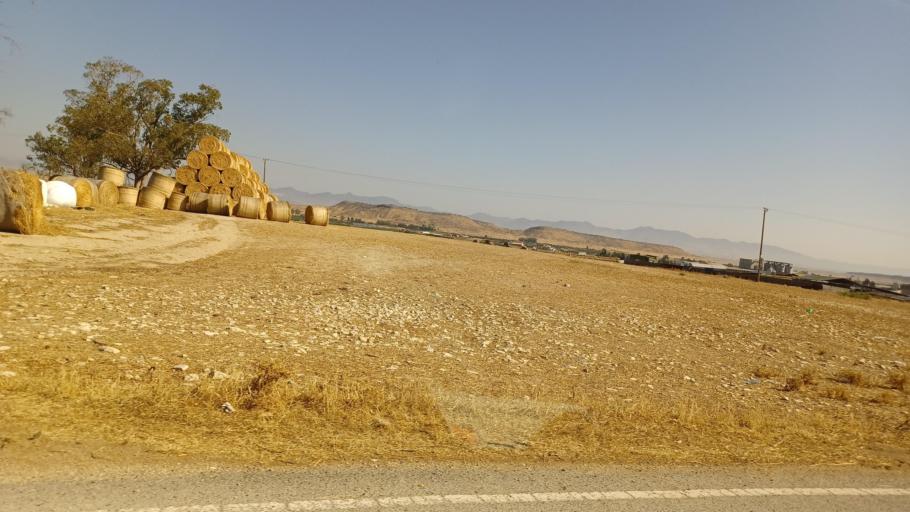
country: CY
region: Larnaka
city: Athienou
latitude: 35.0475
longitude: 33.5189
